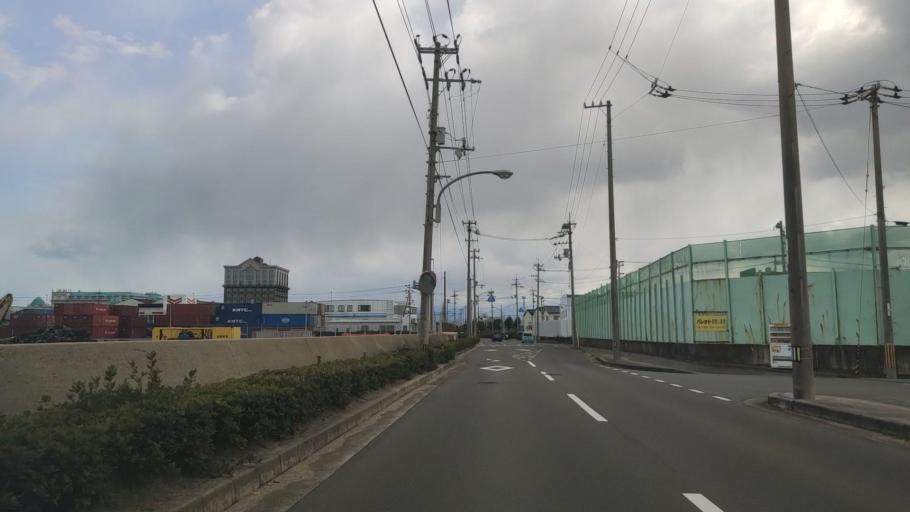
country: JP
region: Ehime
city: Saijo
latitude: 34.0506
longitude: 133.0245
